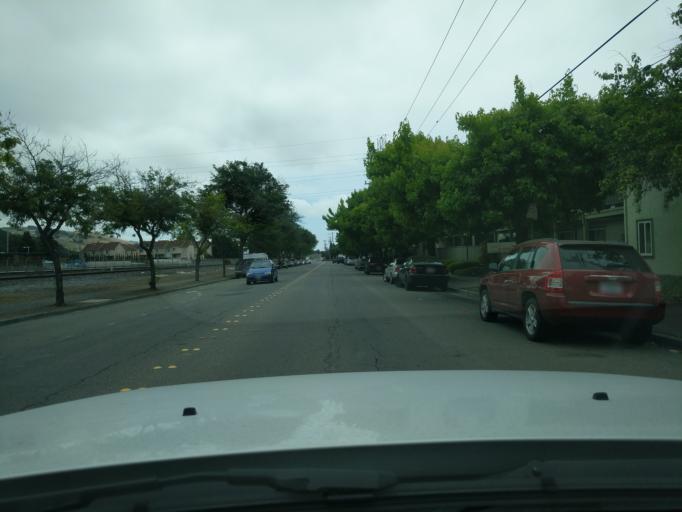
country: US
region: California
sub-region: Alameda County
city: Hayward
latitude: 37.6585
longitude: -122.0768
